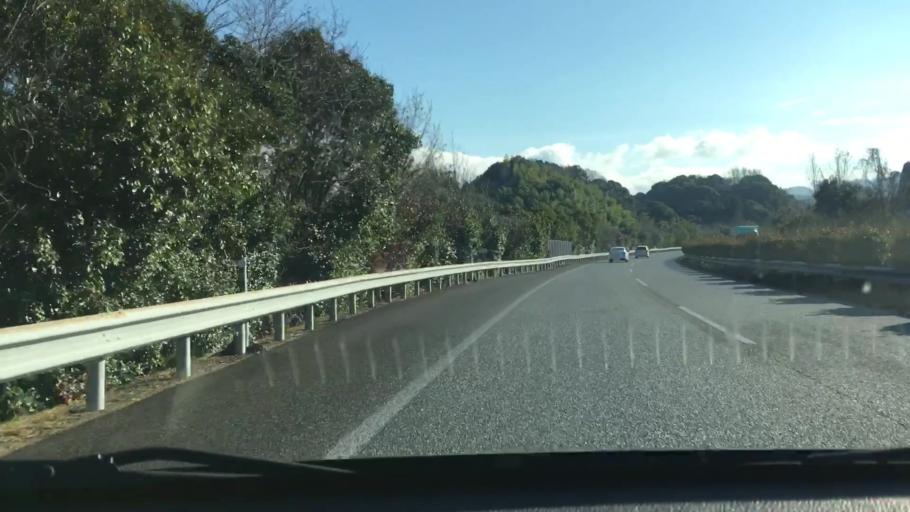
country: JP
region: Kumamoto
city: Hitoyoshi
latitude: 32.1959
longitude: 130.7778
